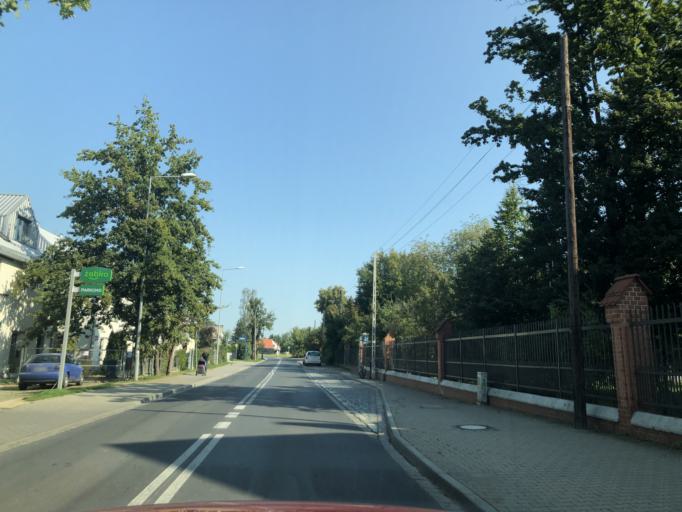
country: PL
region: Lower Silesian Voivodeship
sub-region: Powiat wroclawski
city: Smolec
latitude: 51.1718
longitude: 16.9029
